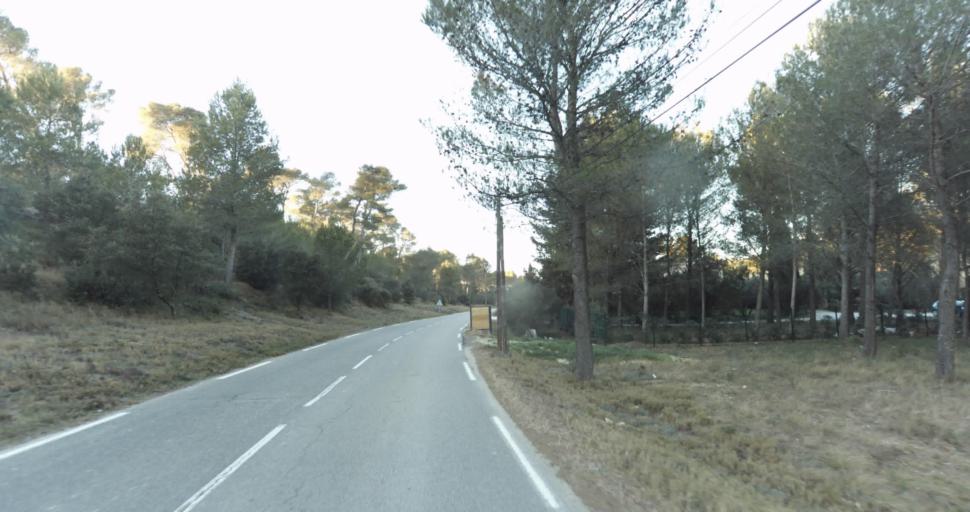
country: FR
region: Provence-Alpes-Cote d'Azur
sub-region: Departement des Bouches-du-Rhone
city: Barbentane
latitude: 43.8926
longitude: 4.7427
